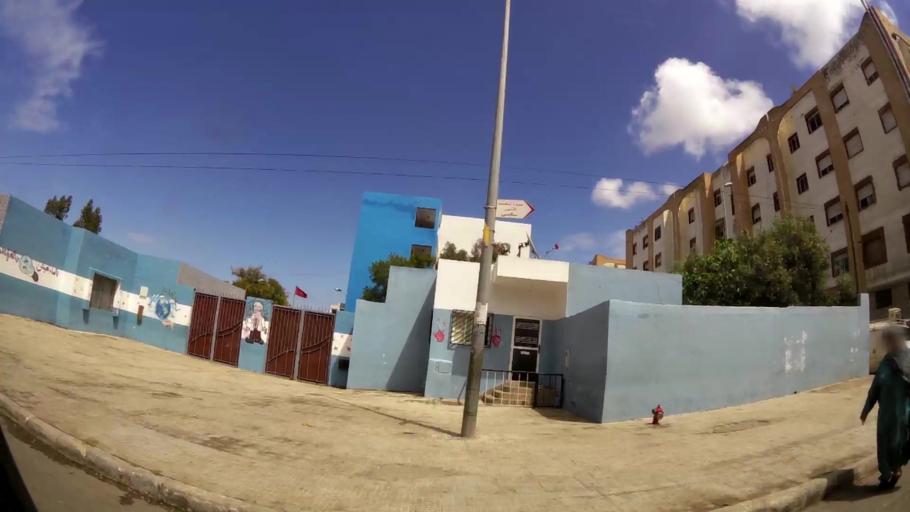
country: MA
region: Grand Casablanca
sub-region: Mediouna
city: Tit Mellil
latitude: 33.6033
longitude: -7.4813
